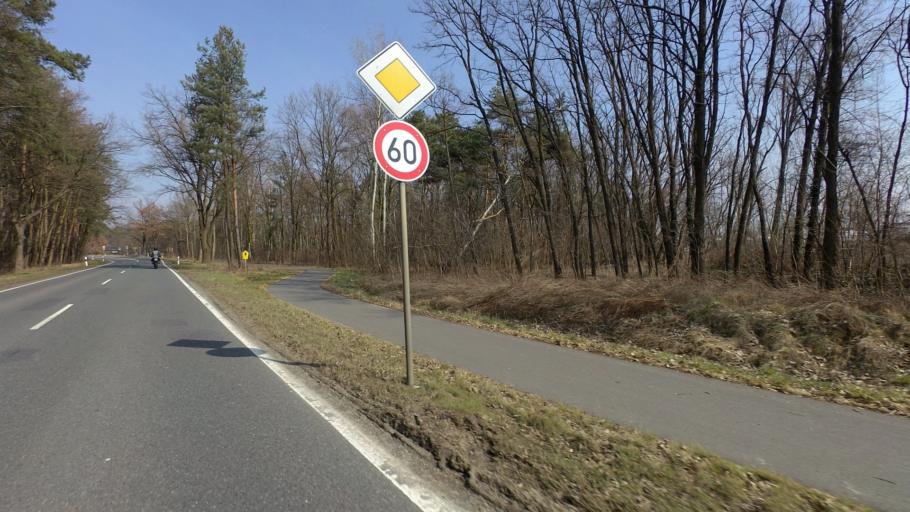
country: DE
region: Brandenburg
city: Werder
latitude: 52.4063
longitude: 12.9065
